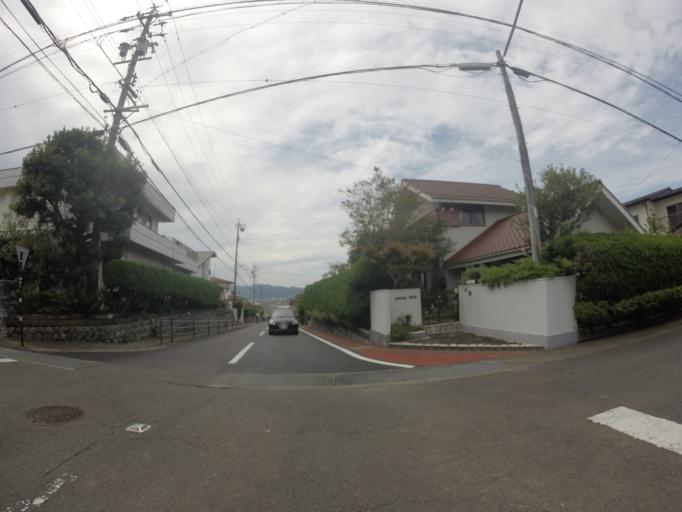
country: JP
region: Shizuoka
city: Shizuoka-shi
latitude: 34.9562
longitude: 138.4312
